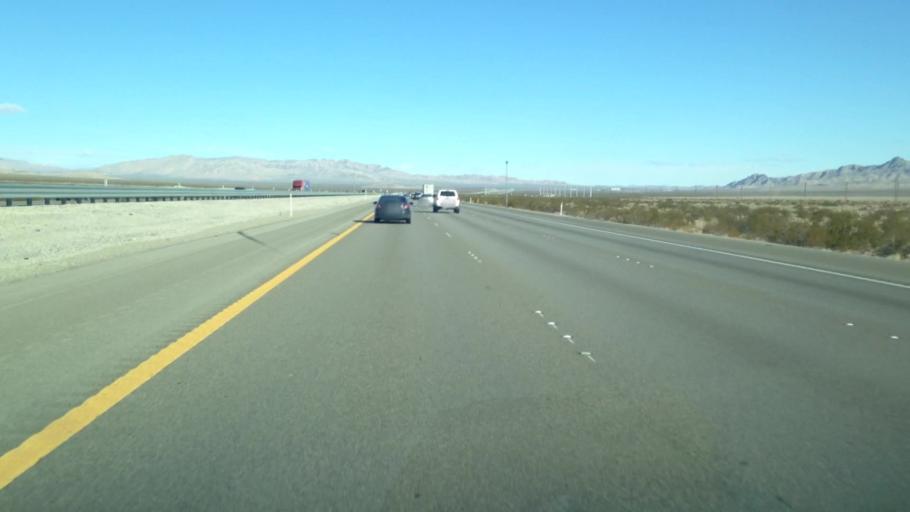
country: US
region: Nevada
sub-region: Clark County
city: Sandy Valley
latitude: 35.6644
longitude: -115.3793
